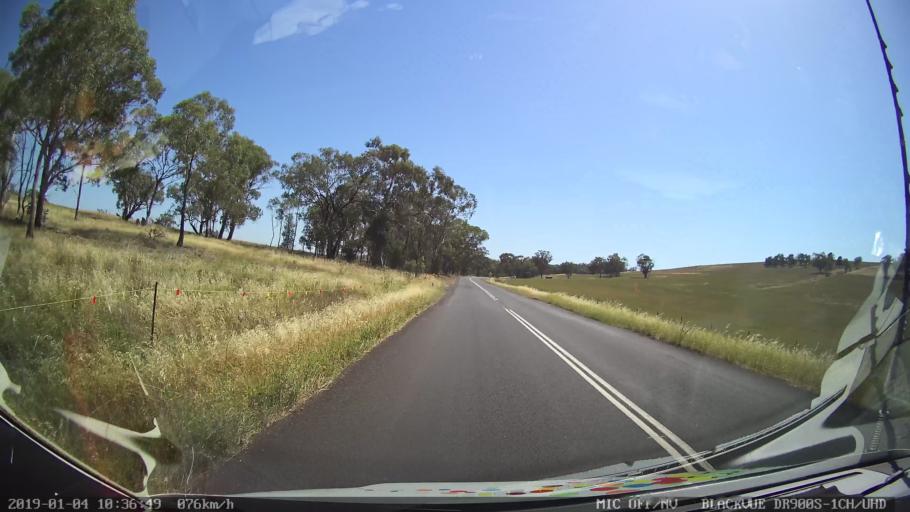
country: AU
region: New South Wales
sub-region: Cabonne
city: Canowindra
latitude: -33.3008
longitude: 148.6884
